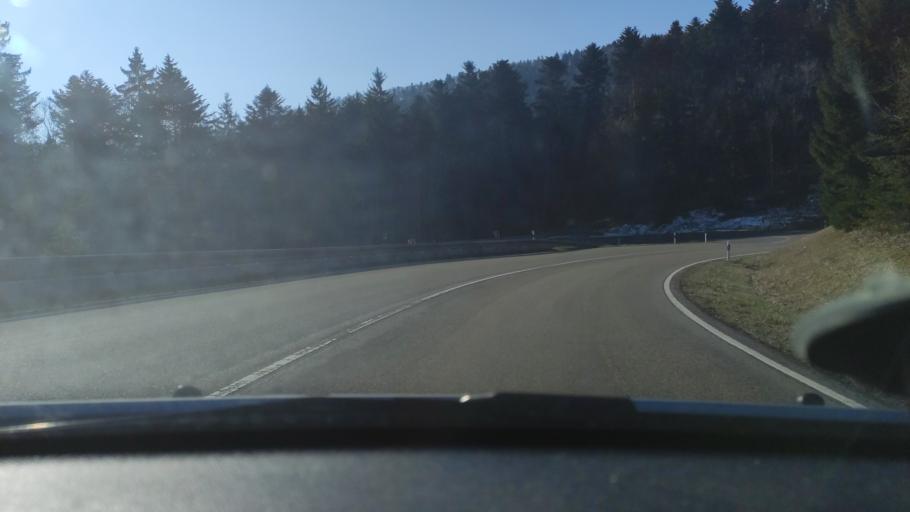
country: DE
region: Baden-Wuerttemberg
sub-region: Tuebingen Region
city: Hausen am Tann
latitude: 48.2230
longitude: 8.8541
